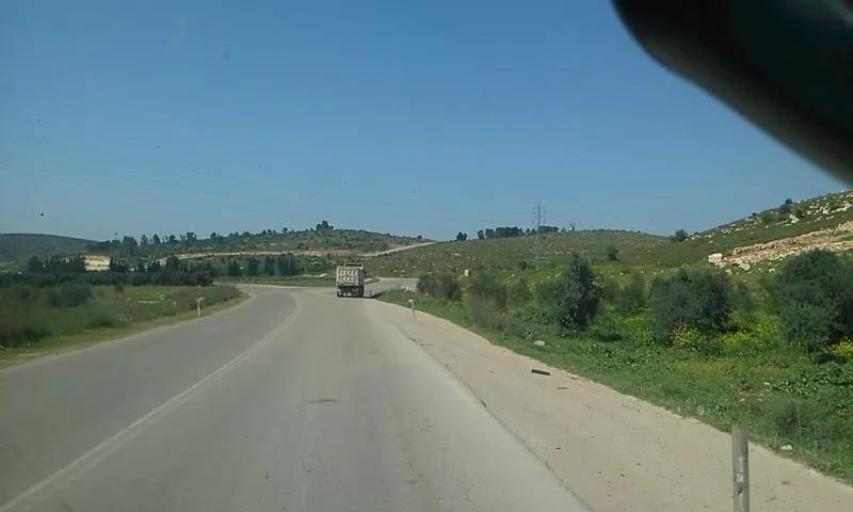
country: PS
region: West Bank
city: Idhna
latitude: 31.5873
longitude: 34.9718
